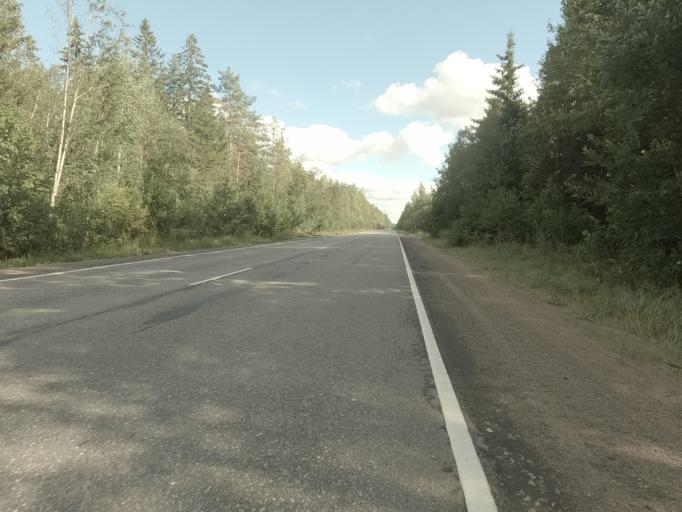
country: RU
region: Leningrad
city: Shcheglovo
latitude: 60.0014
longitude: 30.8697
